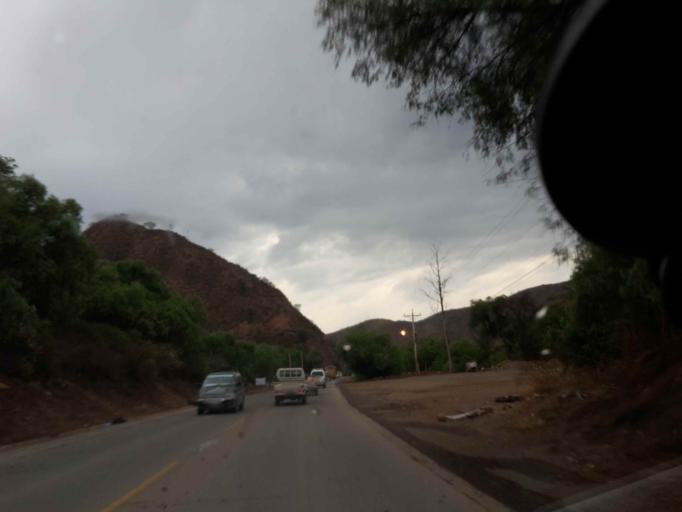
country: BO
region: Cochabamba
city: Sipe Sipe
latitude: -17.5098
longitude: -66.3350
